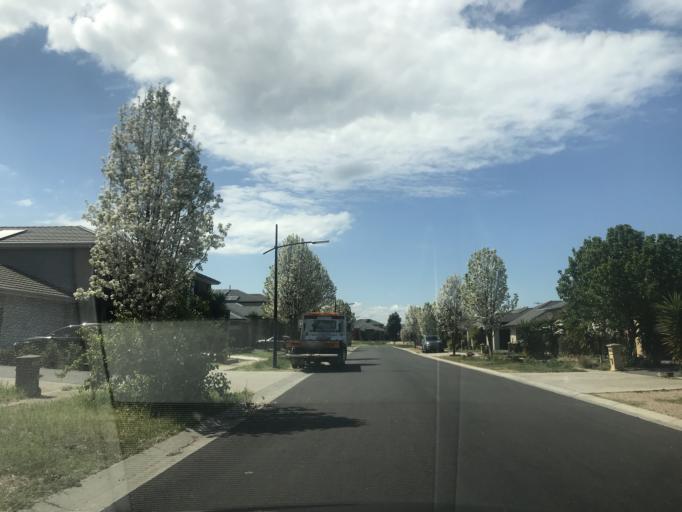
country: AU
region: Victoria
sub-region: Wyndham
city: Hoppers Crossing
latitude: -37.8843
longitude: 144.7194
